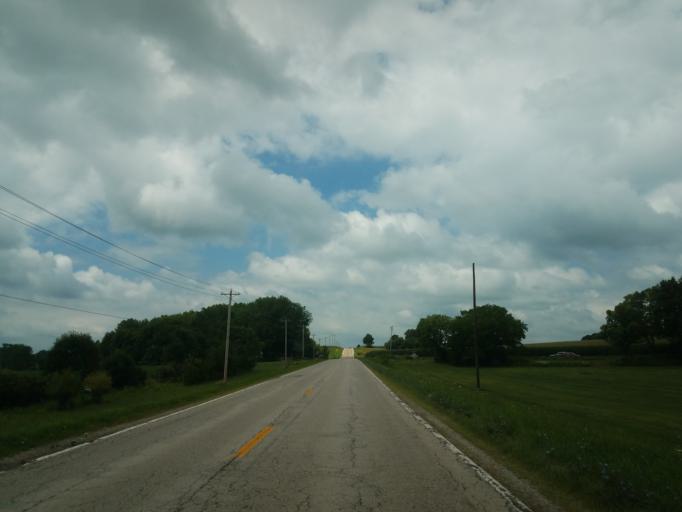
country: US
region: Illinois
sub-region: McLean County
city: Twin Grove
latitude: 40.4587
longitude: -89.0437
